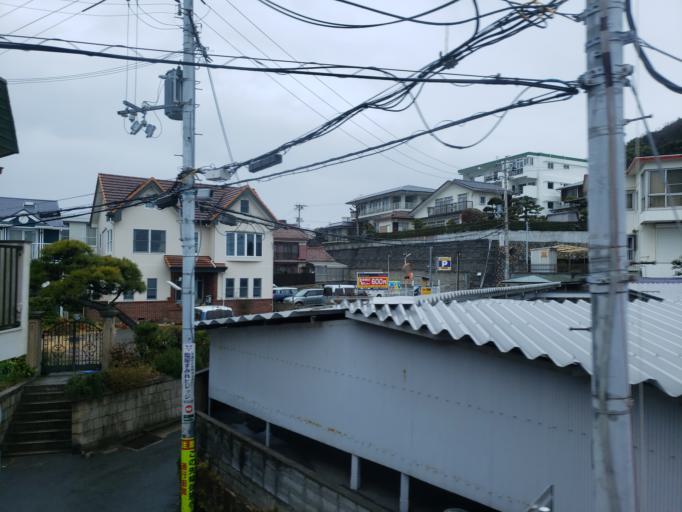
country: JP
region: Hyogo
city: Akashi
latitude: 34.6340
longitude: 135.0841
